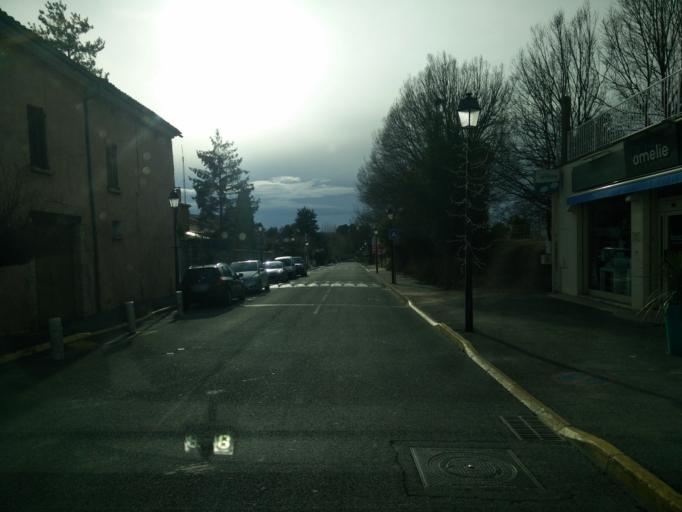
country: FR
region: Provence-Alpes-Cote d'Azur
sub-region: Departement du Var
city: Lorgues
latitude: 43.4918
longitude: 6.3571
